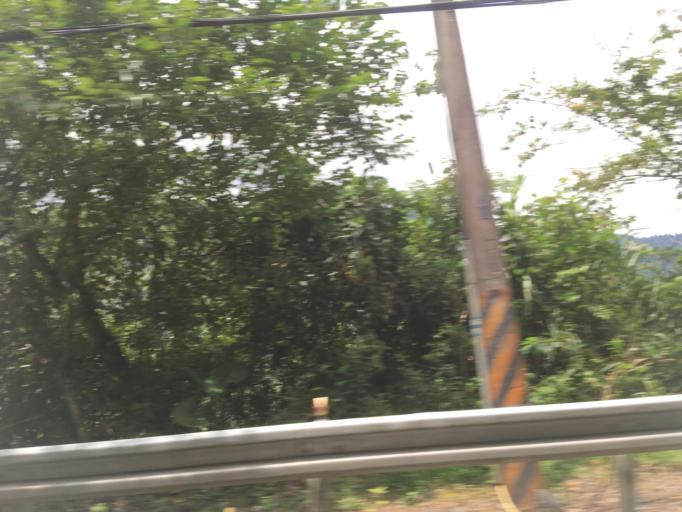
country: TW
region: Taiwan
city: Daxi
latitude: 24.4754
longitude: 121.4182
